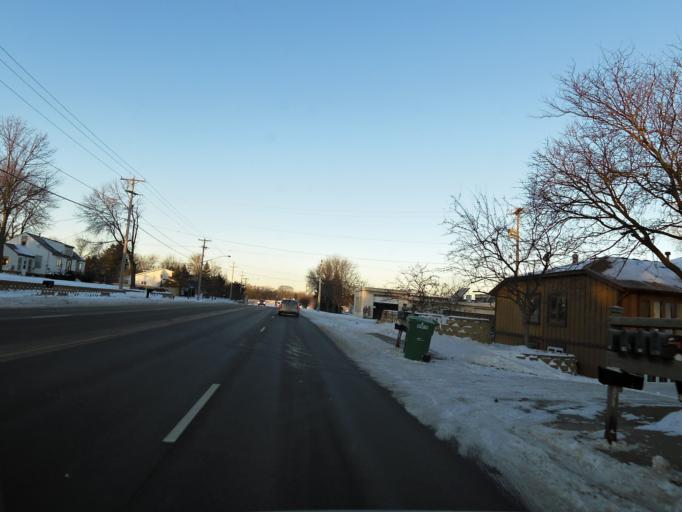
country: US
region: Minnesota
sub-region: Scott County
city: Prior Lake
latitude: 44.7174
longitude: -93.4166
